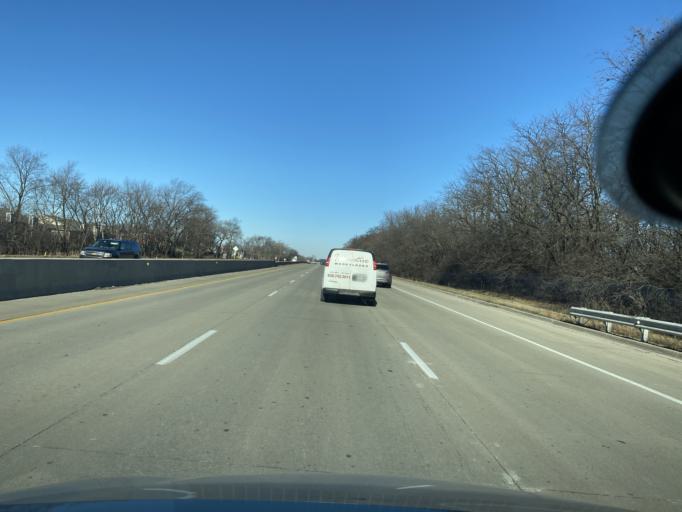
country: US
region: Illinois
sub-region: DuPage County
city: Willowbrook
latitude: 41.7770
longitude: -87.9466
